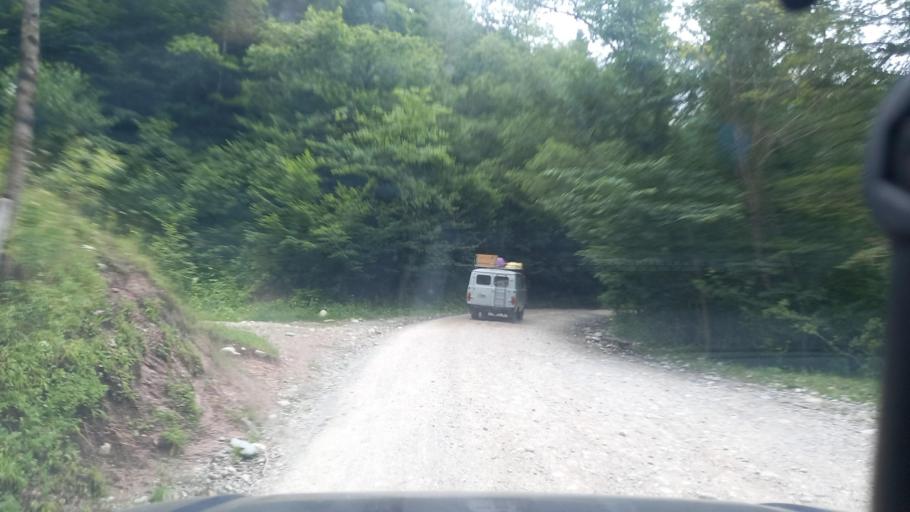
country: RU
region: Karachayevo-Cherkesiya
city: Kurdzhinovo
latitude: 43.8180
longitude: 40.9153
